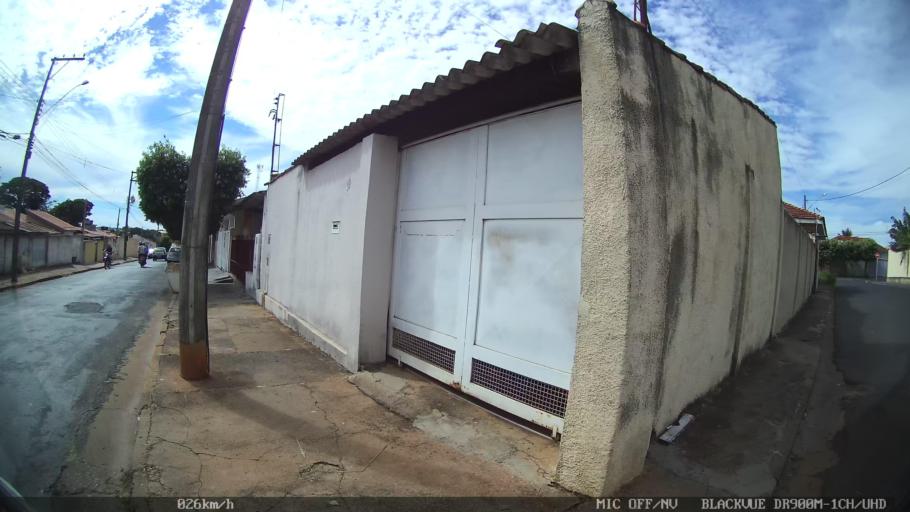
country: BR
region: Sao Paulo
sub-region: Catanduva
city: Catanduva
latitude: -21.1572
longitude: -48.9742
